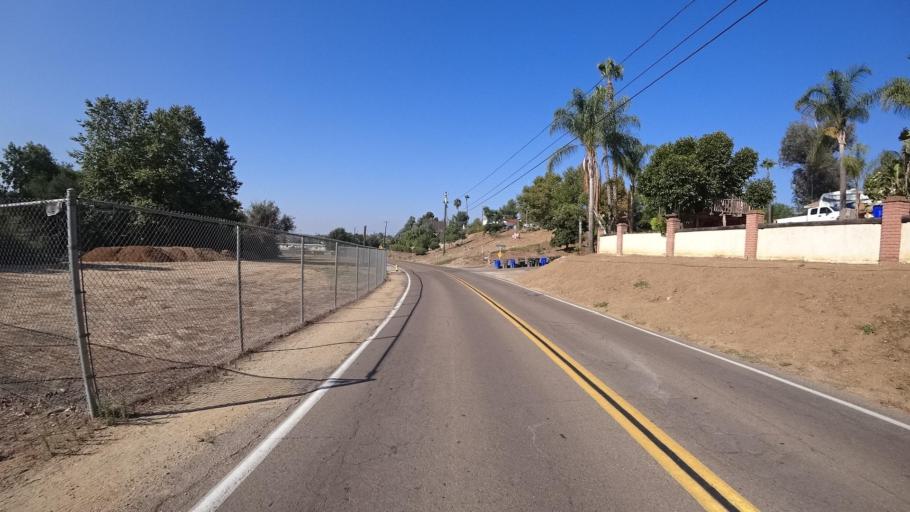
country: US
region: California
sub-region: San Diego County
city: Fallbrook
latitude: 33.3536
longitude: -117.2352
